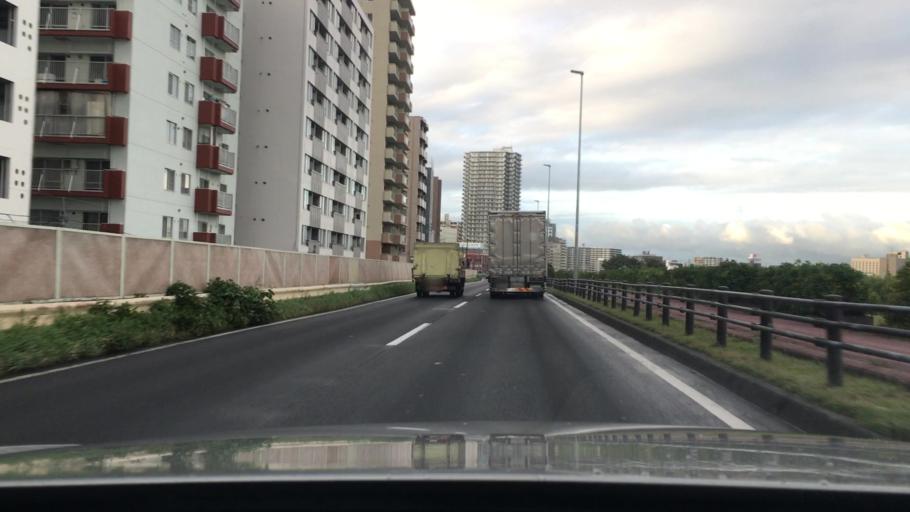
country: JP
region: Hokkaido
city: Sapporo
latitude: 43.0437
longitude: 141.3580
